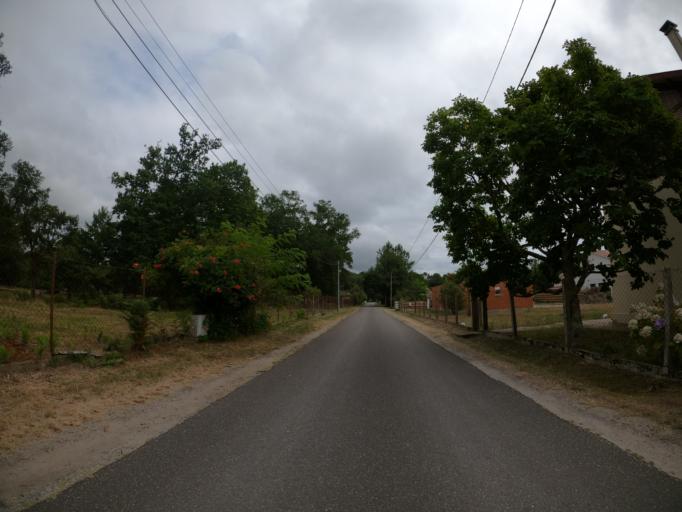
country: FR
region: Aquitaine
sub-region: Departement des Landes
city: Leon
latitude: 43.8846
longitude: -1.3020
